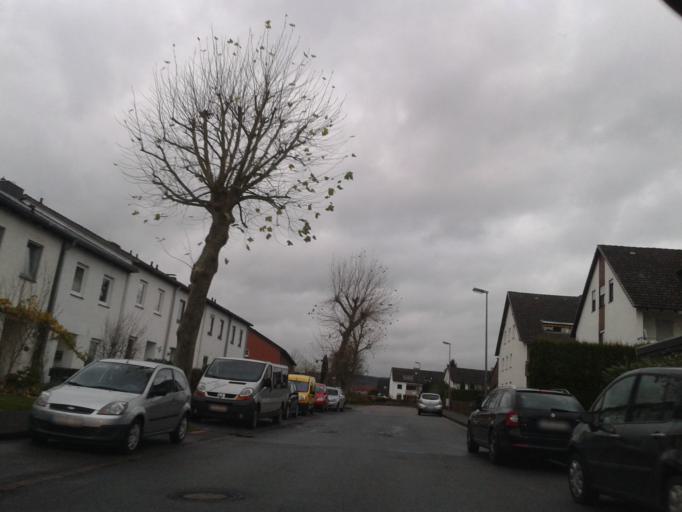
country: DE
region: North Rhine-Westphalia
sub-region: Regierungsbezirk Detmold
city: Blomberg
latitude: 51.9414
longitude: 9.1035
